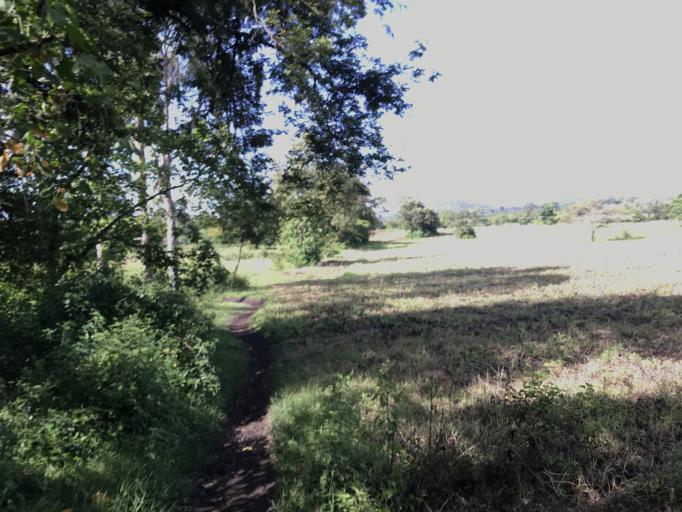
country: TZ
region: Arusha
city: Usa River
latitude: -3.3953
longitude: 36.7970
